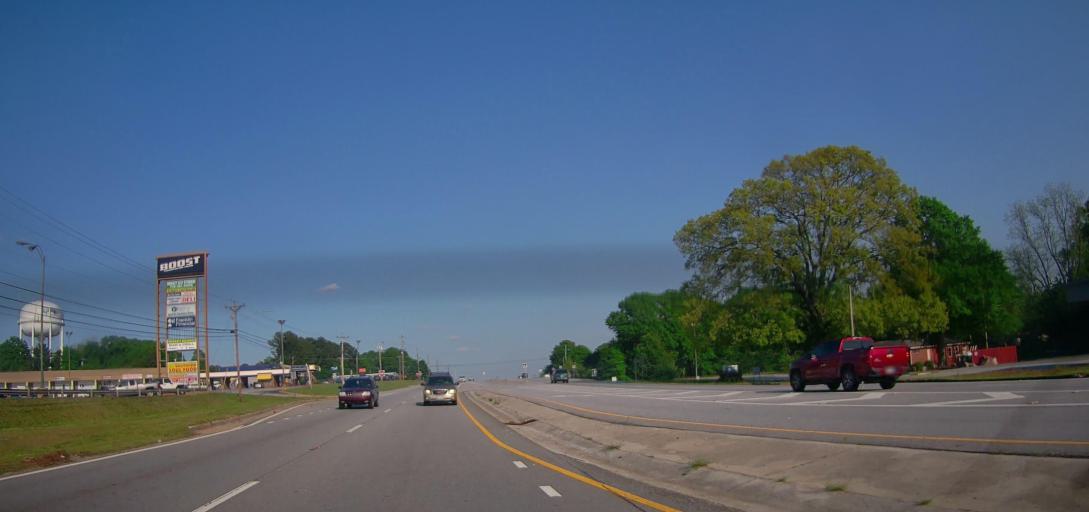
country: US
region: Georgia
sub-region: Newton County
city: Covington
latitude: 33.6022
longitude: -83.8424
